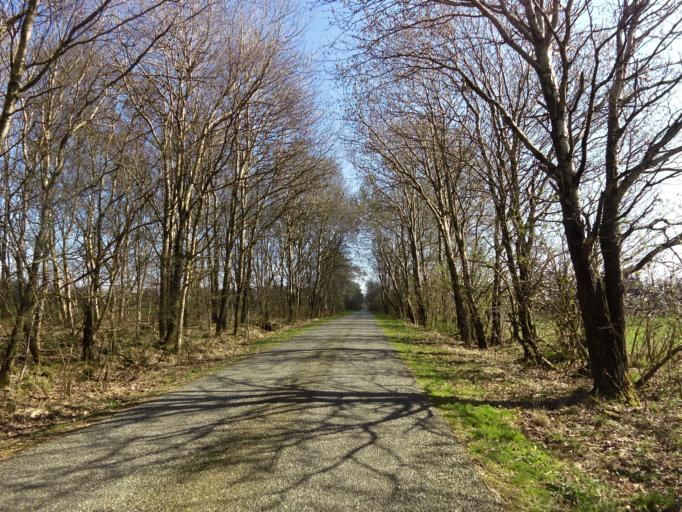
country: DK
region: South Denmark
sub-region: Esbjerg Kommune
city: Ribe
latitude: 55.3449
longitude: 8.8484
